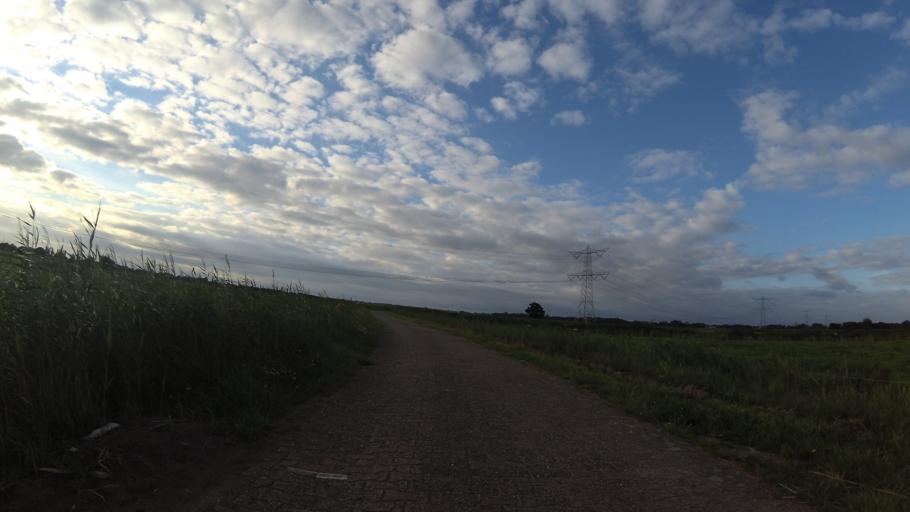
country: NL
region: North Brabant
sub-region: Gemeente Breda
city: Hoge Vucht
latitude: 51.6303
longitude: 4.7850
